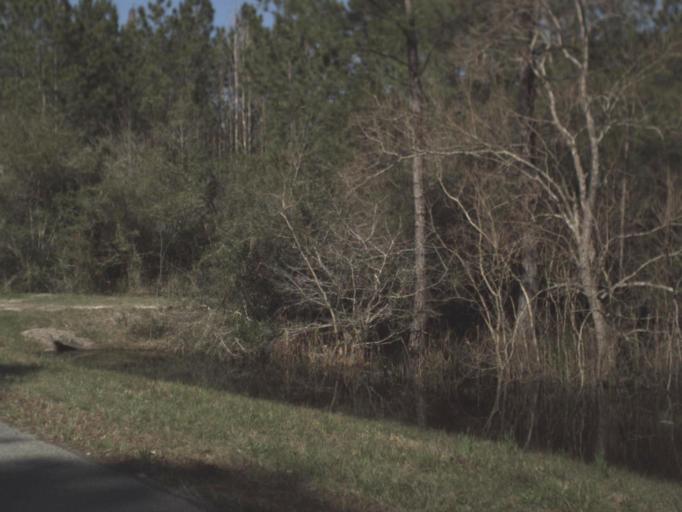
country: US
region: Florida
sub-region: Gulf County
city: Wewahitchka
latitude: 30.0114
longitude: -85.1757
